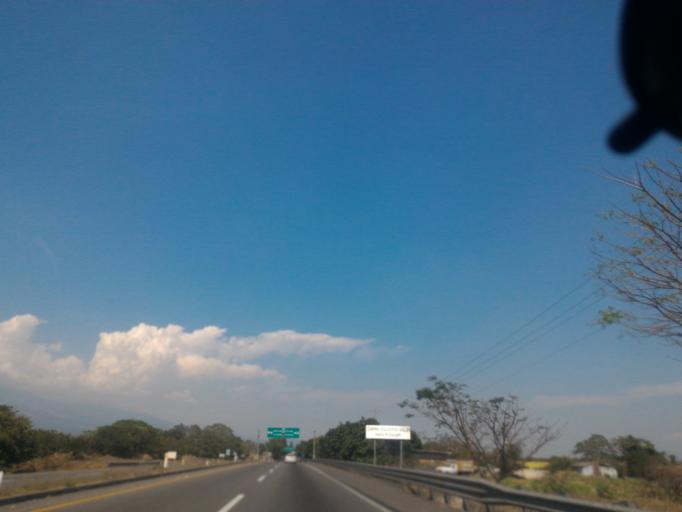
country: MX
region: Colima
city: Queseria
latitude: 19.3580
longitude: -103.5648
